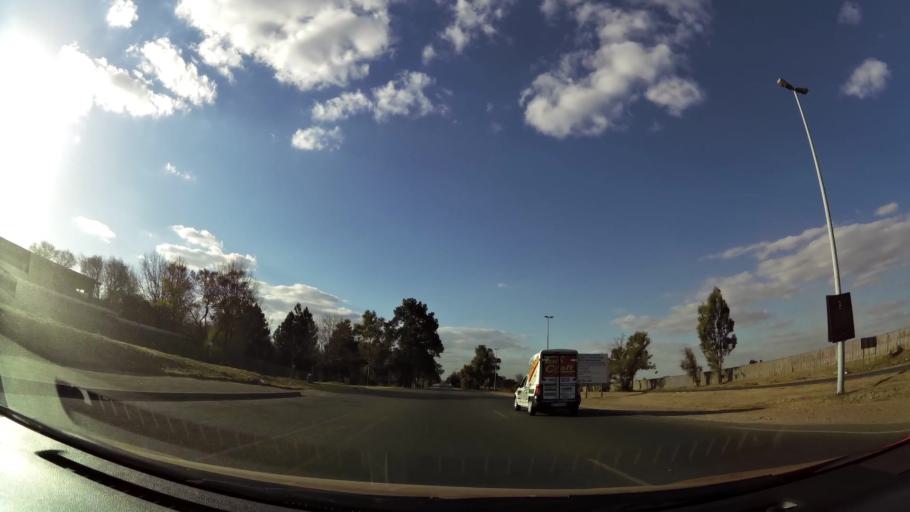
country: ZA
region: Gauteng
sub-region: City of Johannesburg Metropolitan Municipality
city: Midrand
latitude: -25.9810
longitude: 28.1331
